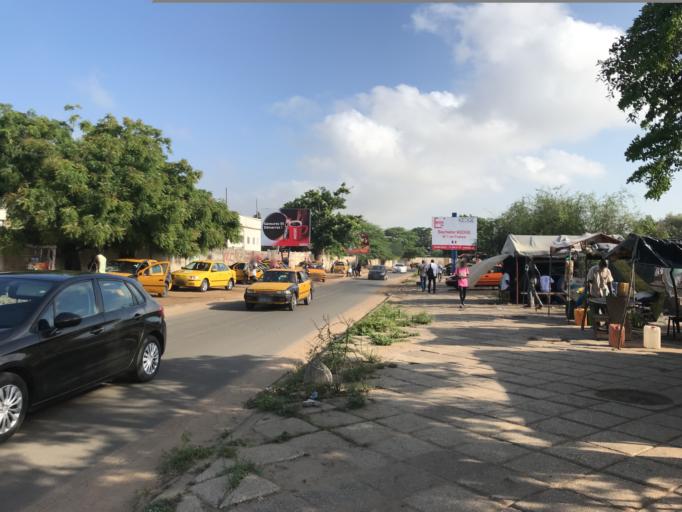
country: SN
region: Dakar
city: Dakar
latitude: 14.6852
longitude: -17.4608
